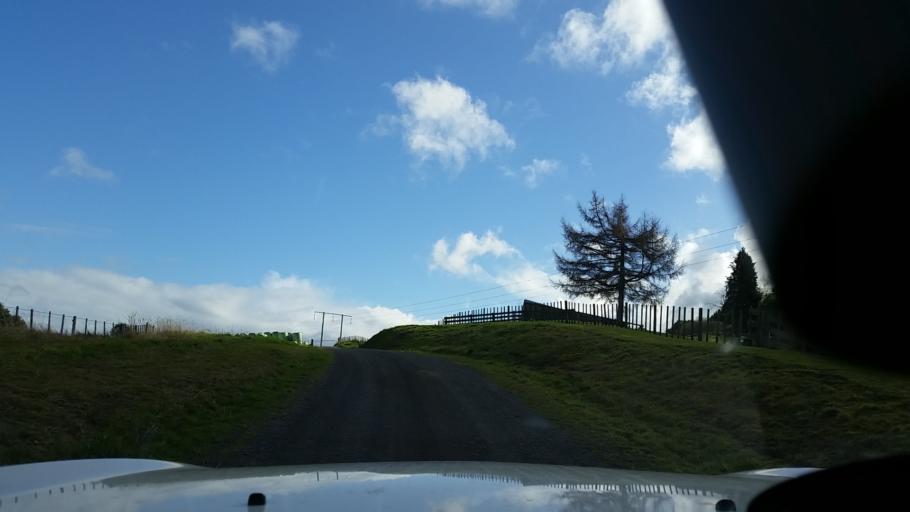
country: NZ
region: Bay of Plenty
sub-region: Rotorua District
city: Rotorua
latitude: -38.0304
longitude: 176.2256
